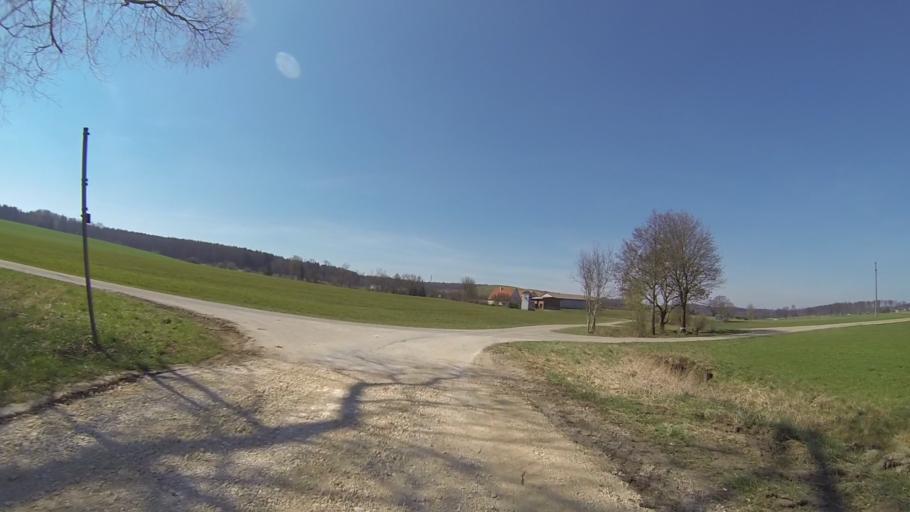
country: DE
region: Baden-Wuerttemberg
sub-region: Regierungsbezirk Stuttgart
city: Nattheim
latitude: 48.6909
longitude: 10.2440
